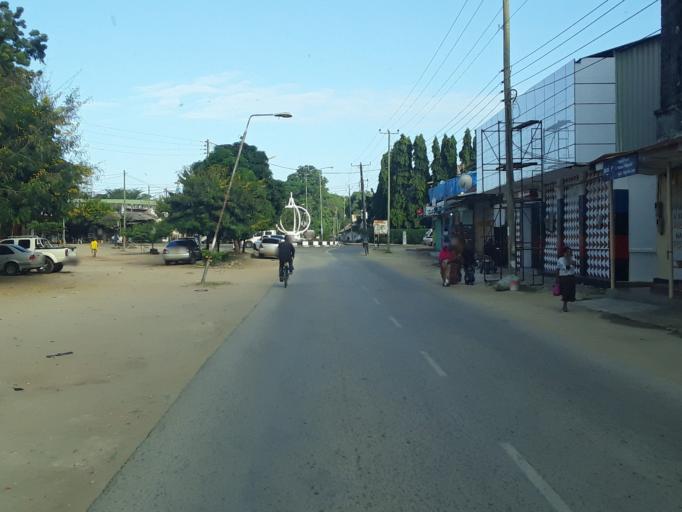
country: TZ
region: Tanga
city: Tanga
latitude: -5.0726
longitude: 39.1029
